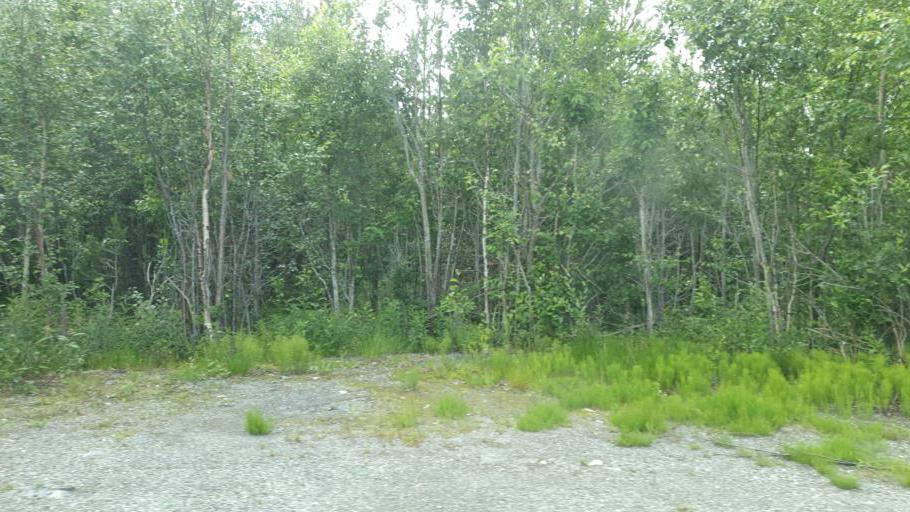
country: NO
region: Sor-Trondelag
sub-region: Oppdal
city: Oppdal
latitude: 62.6493
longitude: 9.8531
